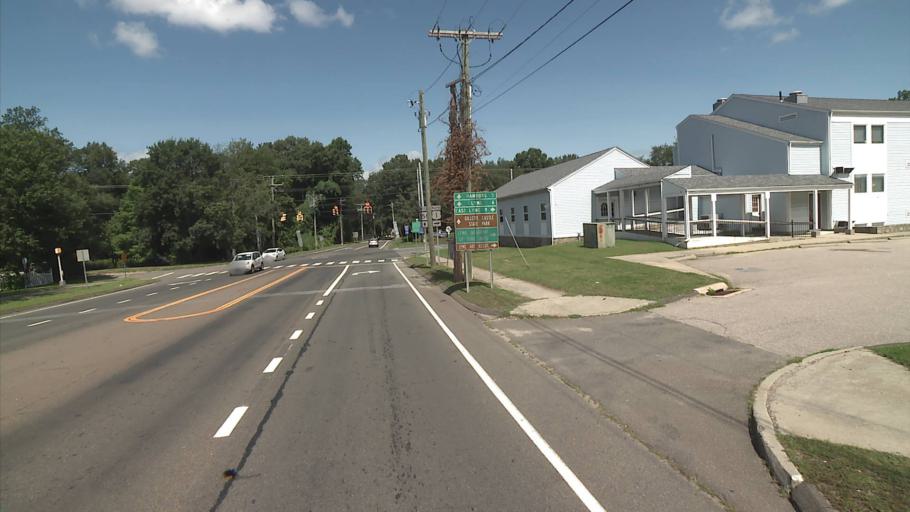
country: US
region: Connecticut
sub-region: Middlesex County
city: Old Saybrook Center
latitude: 41.3217
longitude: -72.3399
